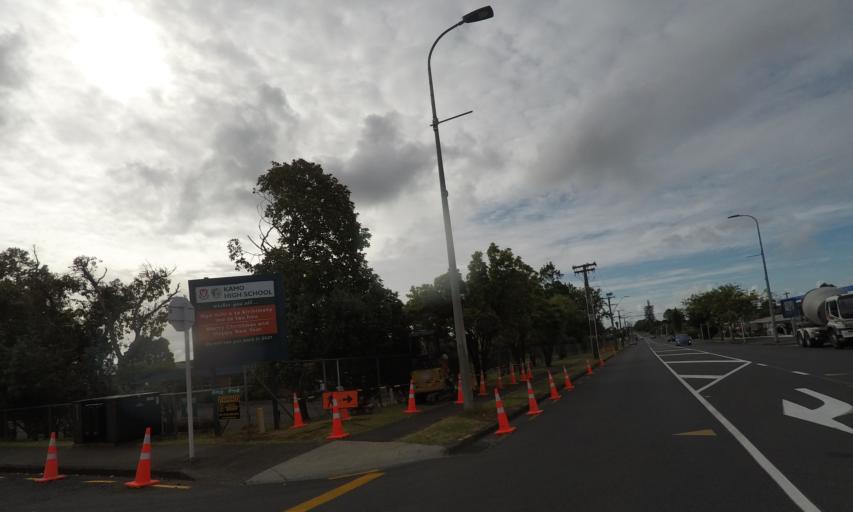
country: NZ
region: Northland
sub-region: Whangarei
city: Whangarei
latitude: -35.6846
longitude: 174.3017
